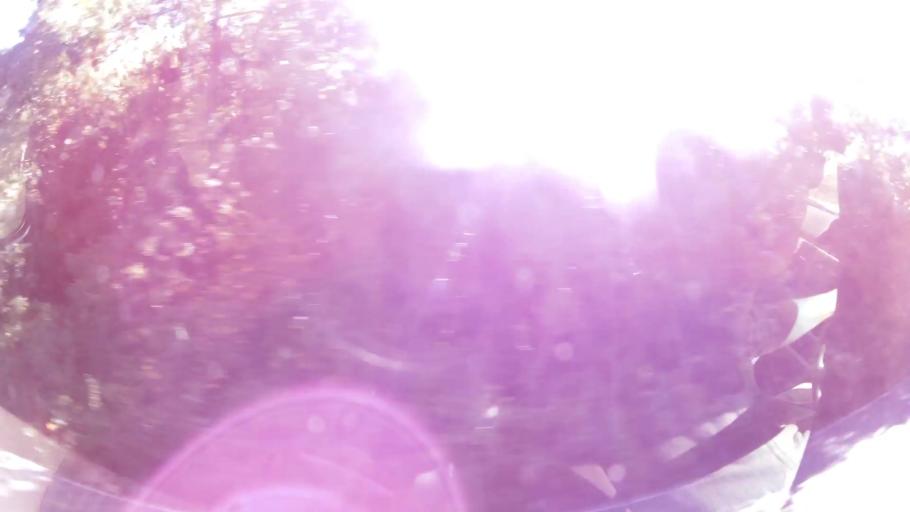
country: GT
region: Solola
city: Solola
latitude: 14.7572
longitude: -91.1757
